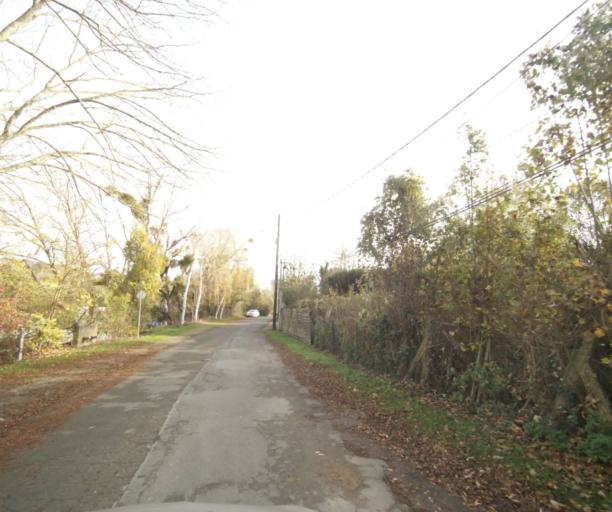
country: FR
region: Ile-de-France
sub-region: Departement du Val-d'Oise
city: Herblay
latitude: 48.9833
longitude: 2.1716
